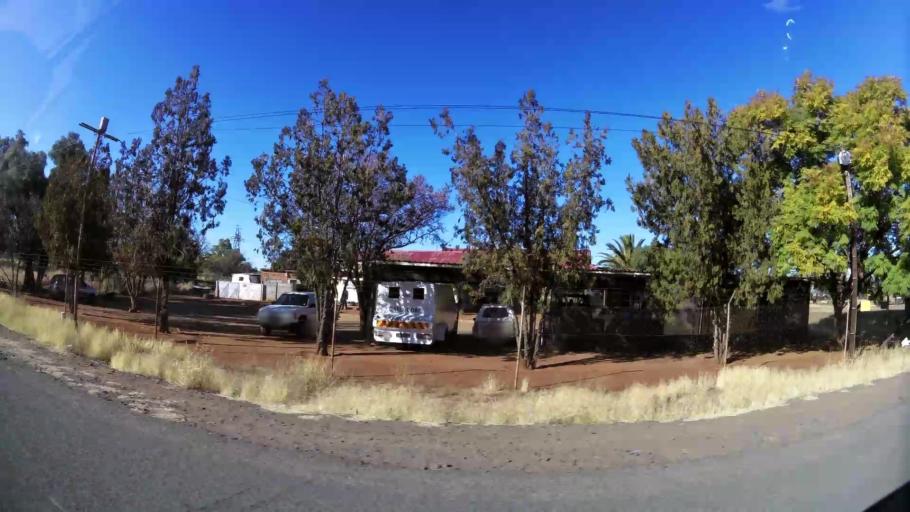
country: ZA
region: Northern Cape
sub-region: Frances Baard District Municipality
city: Kimberley
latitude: -28.7480
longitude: 24.7938
